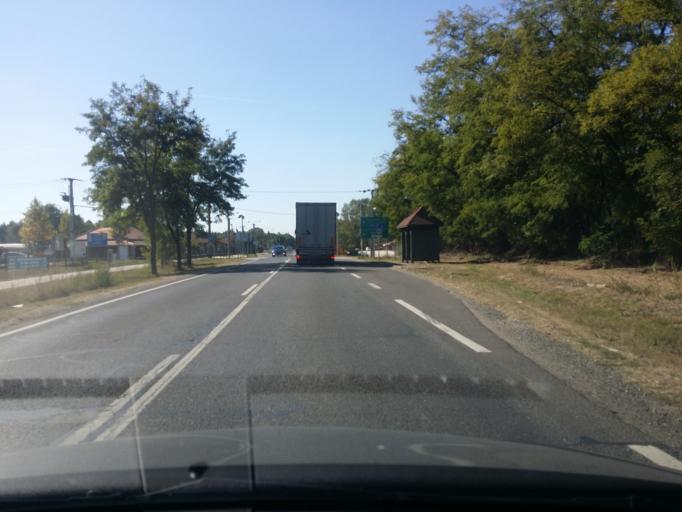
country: HU
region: Bacs-Kiskun
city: Lakitelek
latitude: 46.8684
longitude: 19.9611
